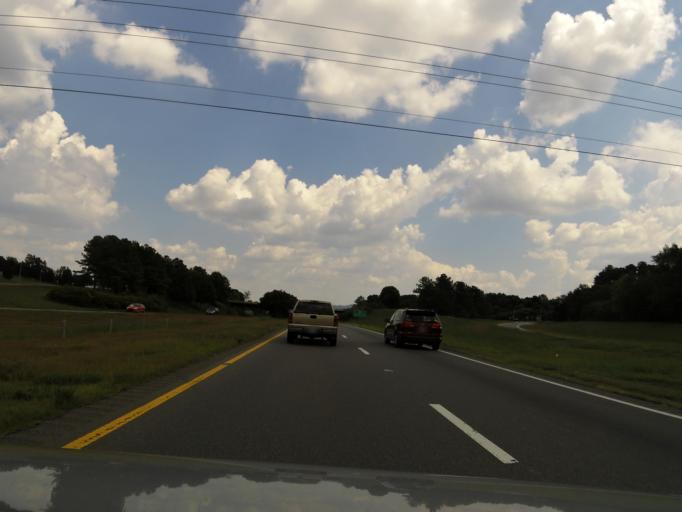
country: US
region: North Carolina
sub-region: Cleveland County
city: Kings Mountain
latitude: 35.2513
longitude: -81.3434
